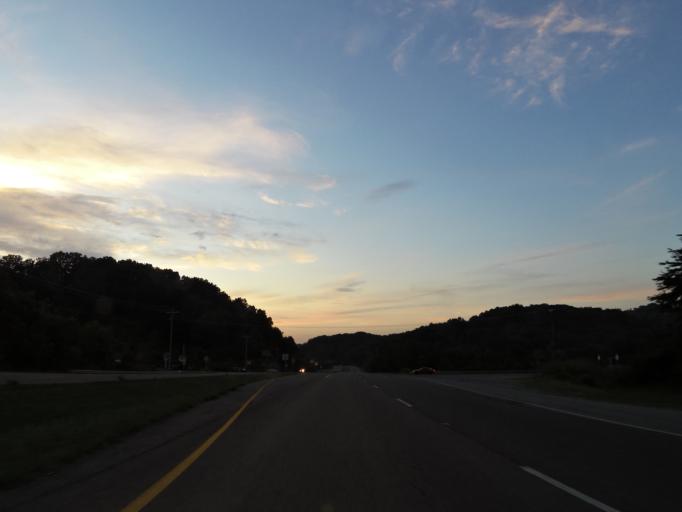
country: US
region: Tennessee
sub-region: Carter County
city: Elizabethton
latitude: 36.3725
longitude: -82.2140
